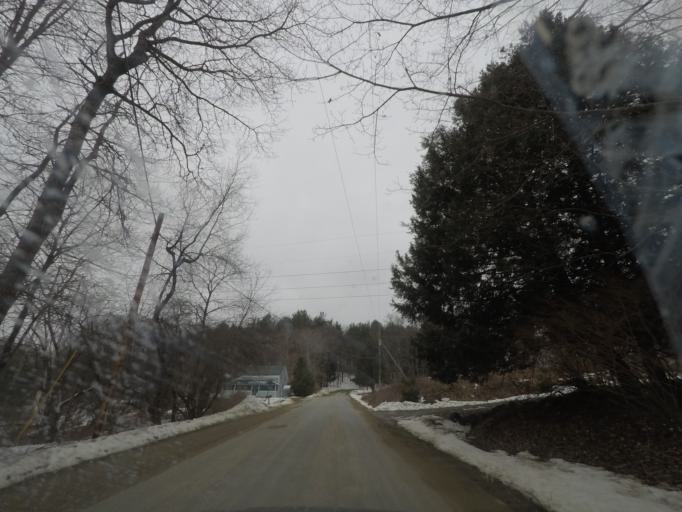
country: US
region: Massachusetts
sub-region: Berkshire County
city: Richmond
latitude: 42.5390
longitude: -73.4056
